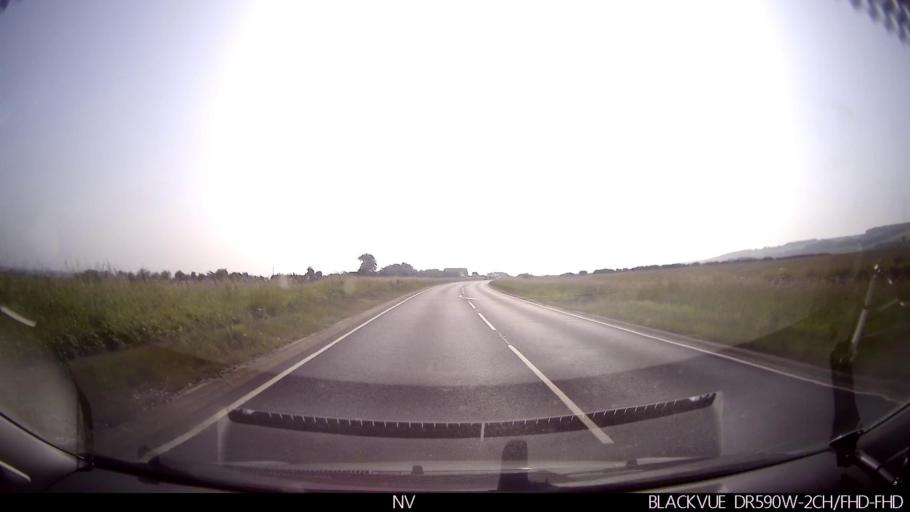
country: GB
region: England
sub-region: North Yorkshire
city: Wintringham
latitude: 54.1791
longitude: -0.5734
